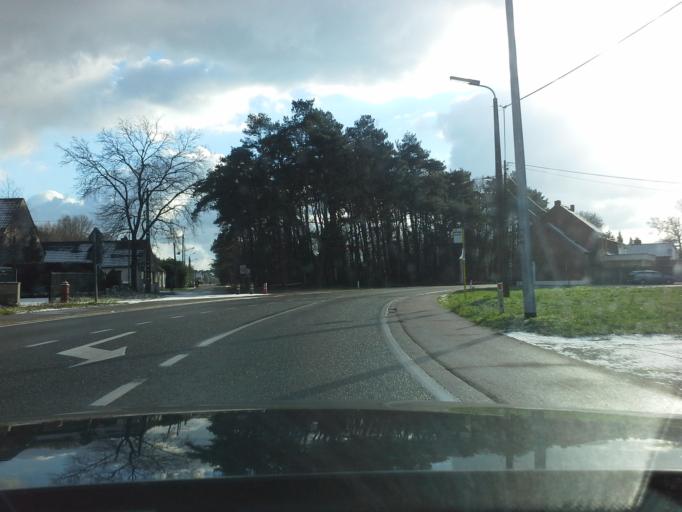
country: BE
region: Flanders
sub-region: Provincie Antwerpen
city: Mol
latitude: 51.1743
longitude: 5.1082
